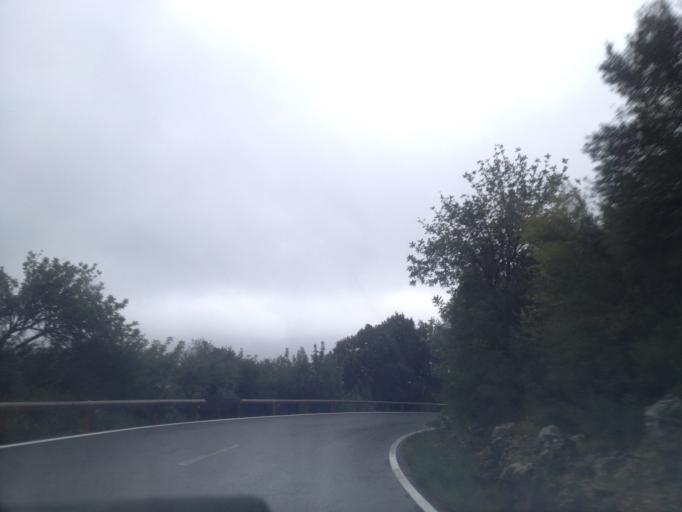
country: ES
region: Balearic Islands
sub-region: Illes Balears
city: Fornalutx
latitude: 39.7866
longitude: 2.7377
